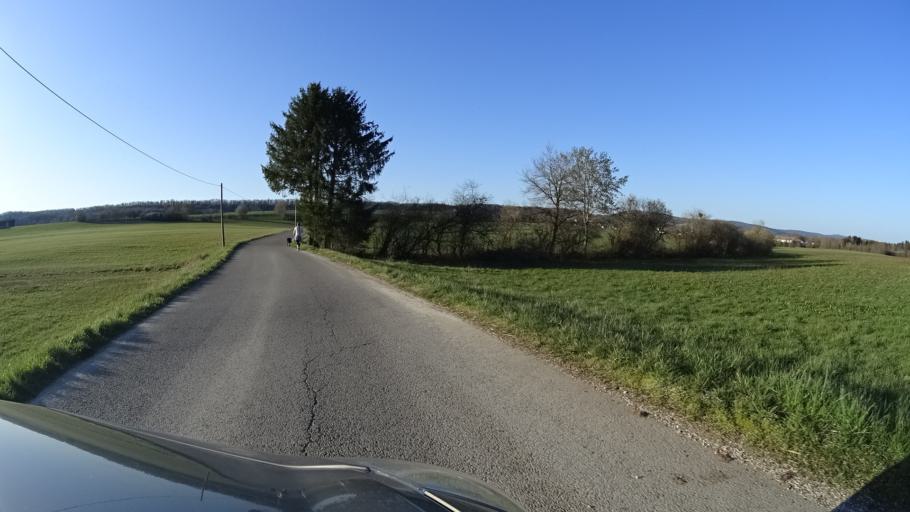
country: FR
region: Franche-Comte
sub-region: Departement du Doubs
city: Morre
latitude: 47.1992
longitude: 6.0616
